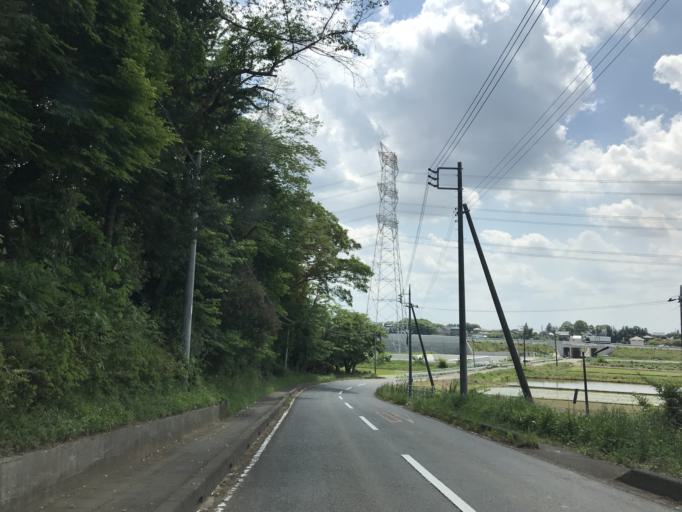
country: JP
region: Ibaraki
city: Mitsukaido
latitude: 36.0629
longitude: 140.0402
